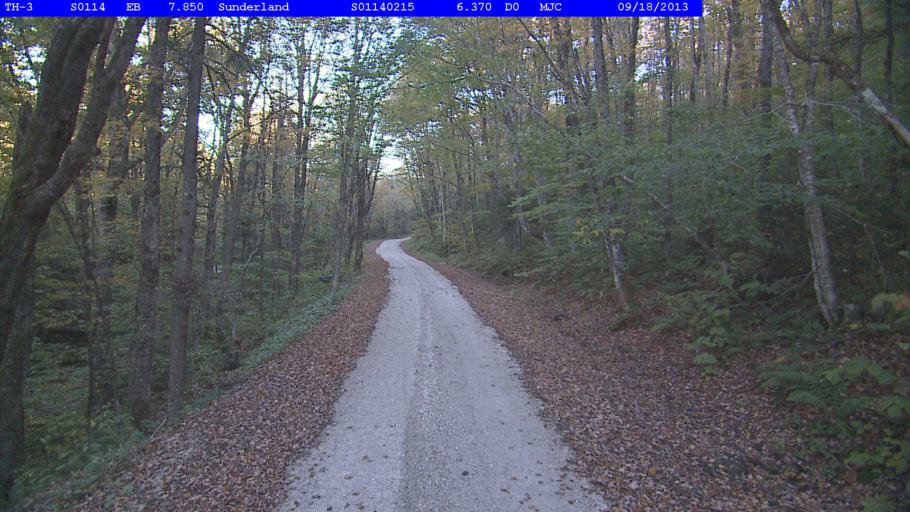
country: US
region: Vermont
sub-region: Bennington County
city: Arlington
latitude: 43.0548
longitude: -73.0608
